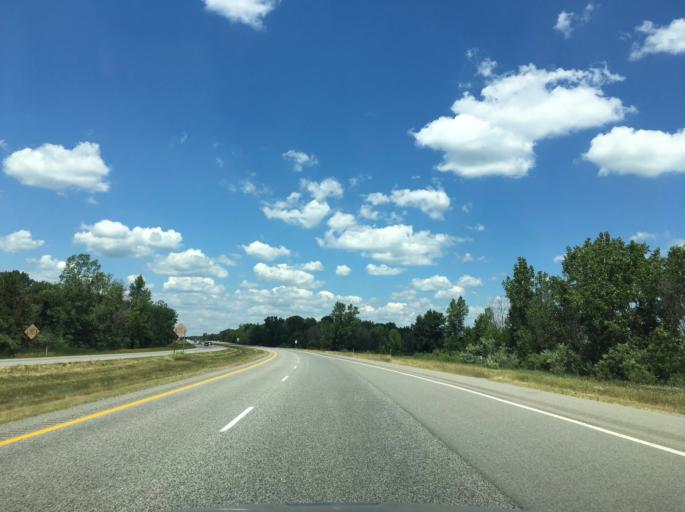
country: US
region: Michigan
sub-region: Midland County
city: Midland
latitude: 43.6453
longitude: -84.1910
